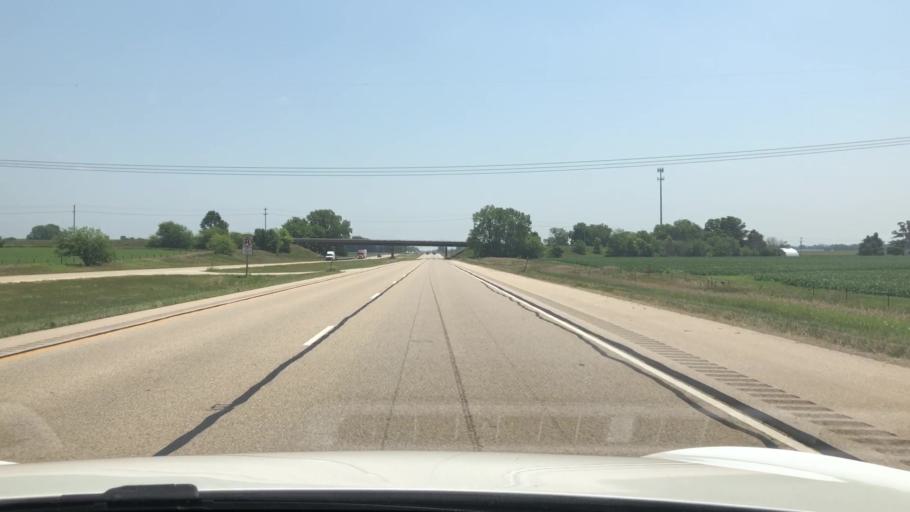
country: US
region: Illinois
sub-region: McLean County
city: Downs
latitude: 40.4161
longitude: -88.9357
